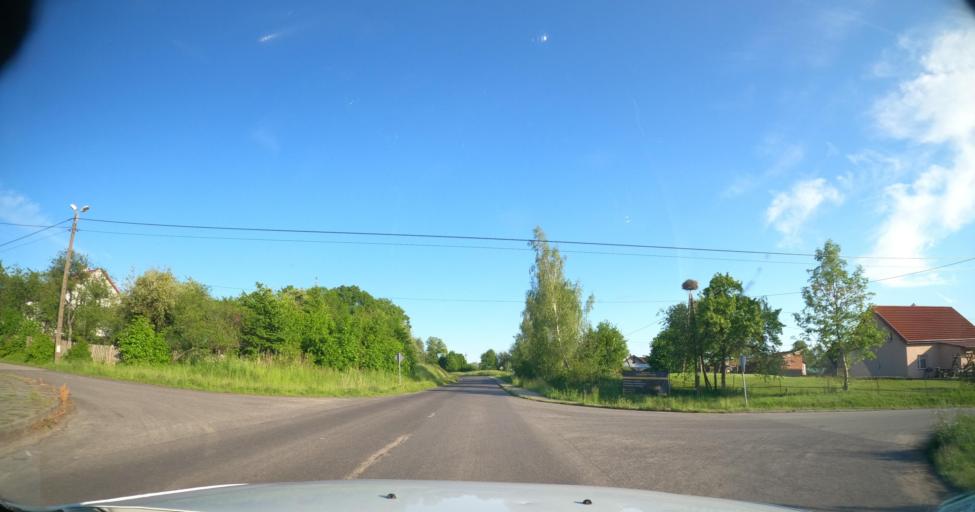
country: PL
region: Warmian-Masurian Voivodeship
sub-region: Powiat braniewski
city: Braniewo
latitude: 54.2695
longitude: 19.9378
